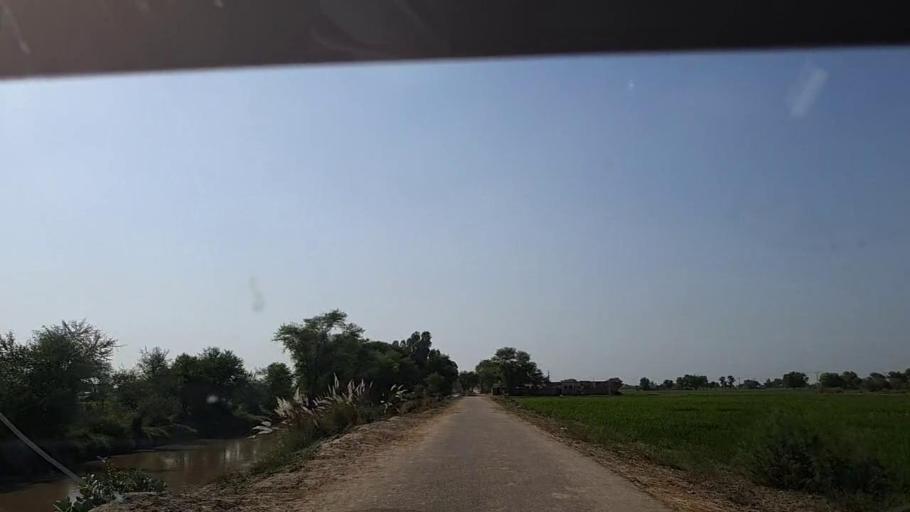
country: PK
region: Sindh
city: Tangwani
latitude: 28.2087
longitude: 69.0268
